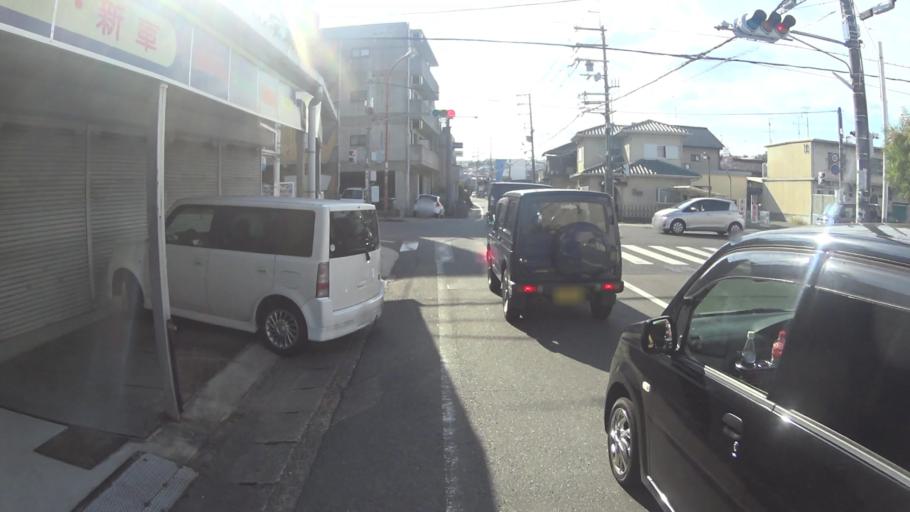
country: JP
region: Kyoto
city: Yawata
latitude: 34.8660
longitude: 135.7065
